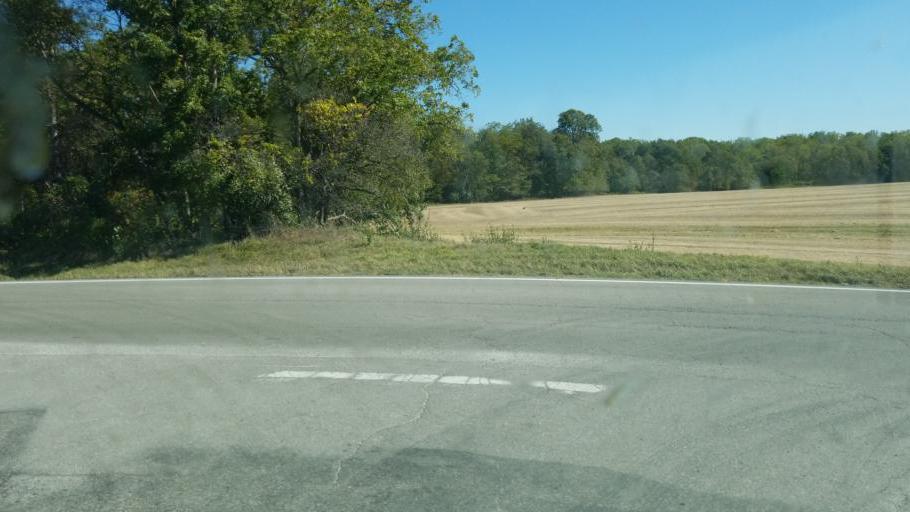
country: US
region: Ohio
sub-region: Huron County
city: Plymouth
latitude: 40.9815
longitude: -82.7095
